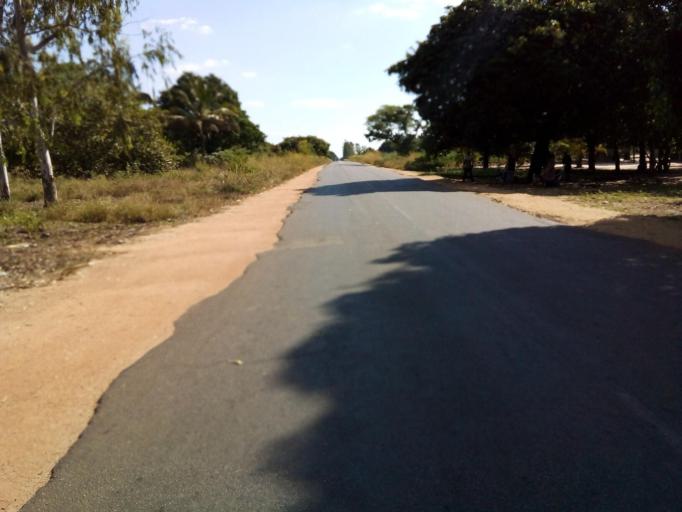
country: MZ
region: Zambezia
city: Quelimane
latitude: -17.5762
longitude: 36.6408
